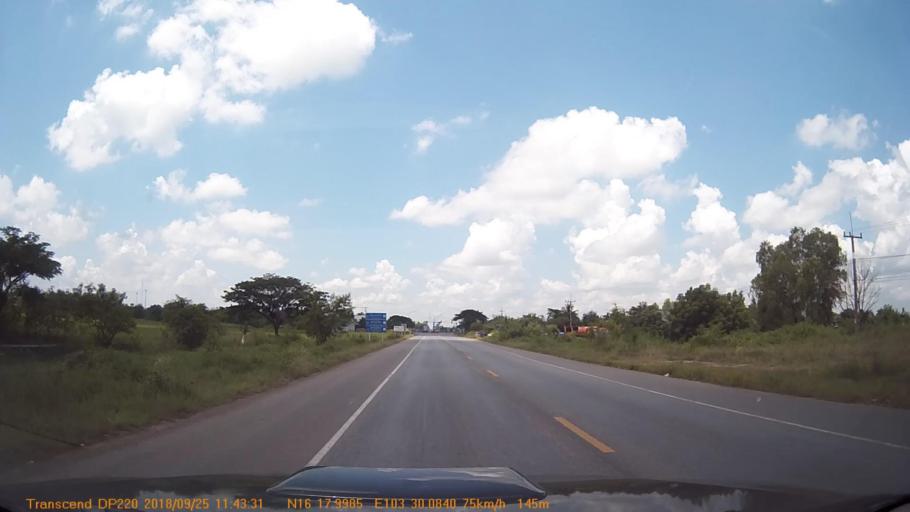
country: TH
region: Kalasin
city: Khong Chai
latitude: 16.2999
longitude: 103.5016
